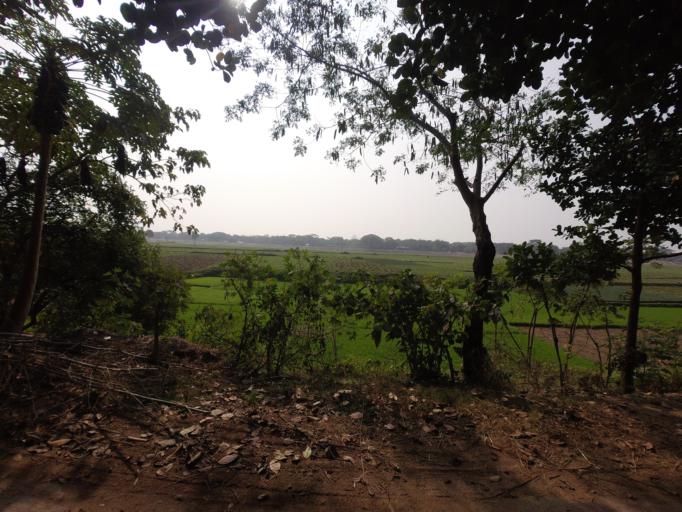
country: BD
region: Dhaka
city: Netrakona
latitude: 25.0128
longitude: 90.6543
